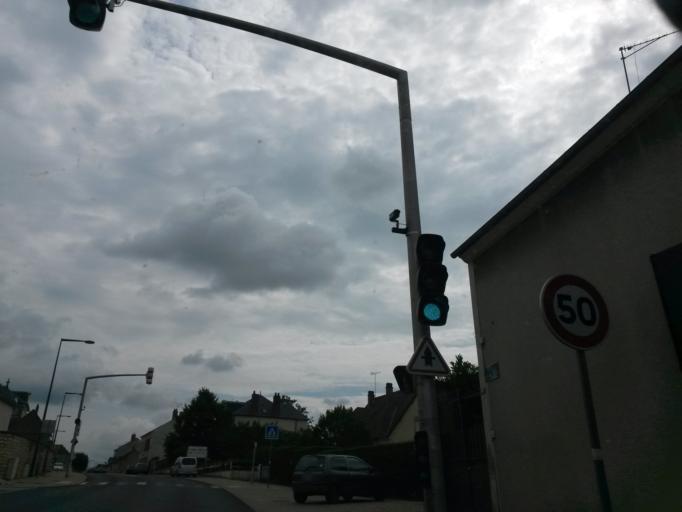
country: FR
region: Bourgogne
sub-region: Departement de la Nievre
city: Coulanges-les-Nevers
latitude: 47.0013
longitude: 3.1793
